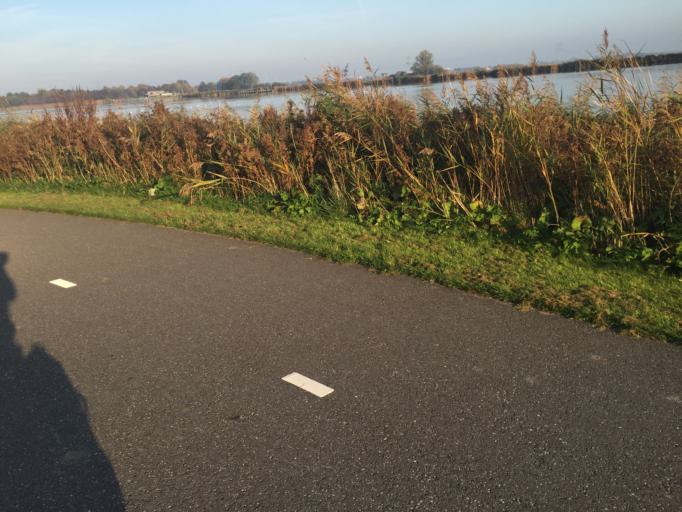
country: NL
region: South Holland
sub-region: Gemeente Lansingerland
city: Bleiswijk
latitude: 52.0045
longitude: 4.5524
